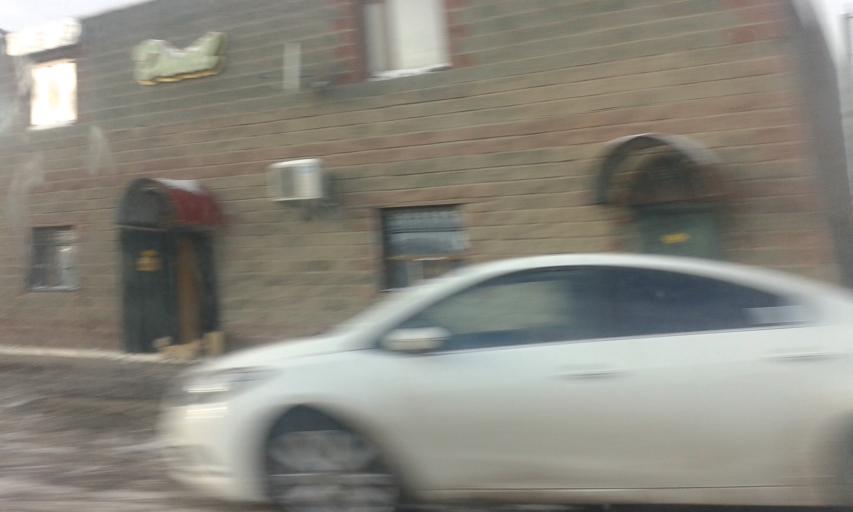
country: KZ
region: Astana Qalasy
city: Astana
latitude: 51.1449
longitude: 71.4594
